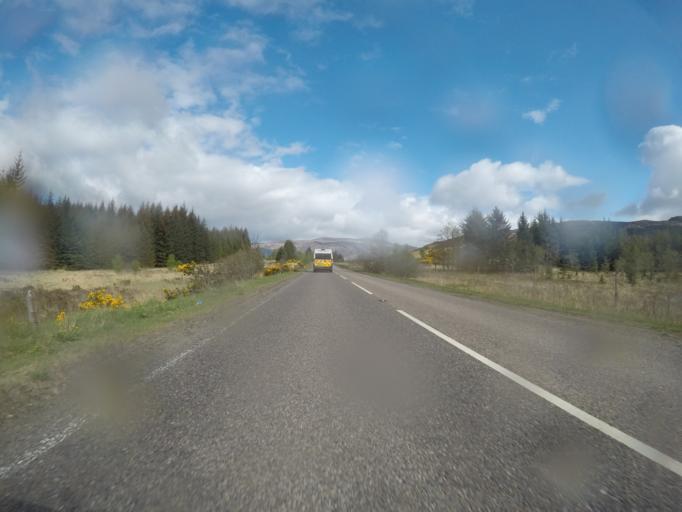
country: GB
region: Scotland
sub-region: Highland
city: Spean Bridge
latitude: 56.9081
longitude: -4.9447
